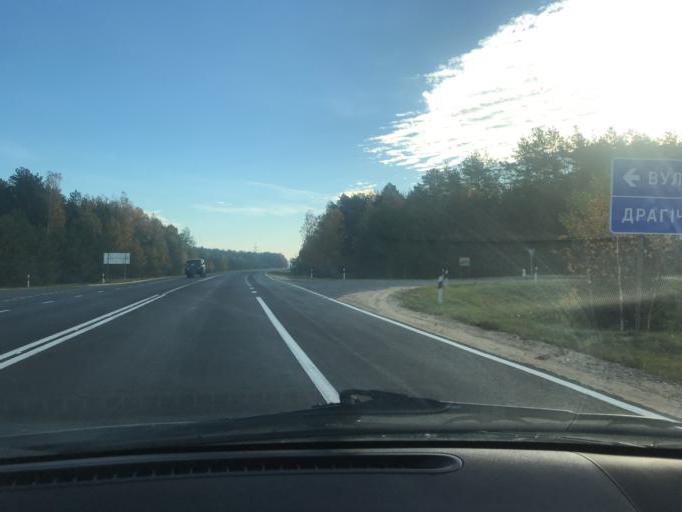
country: BY
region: Brest
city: Drahichyn
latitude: 52.2247
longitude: 25.1403
